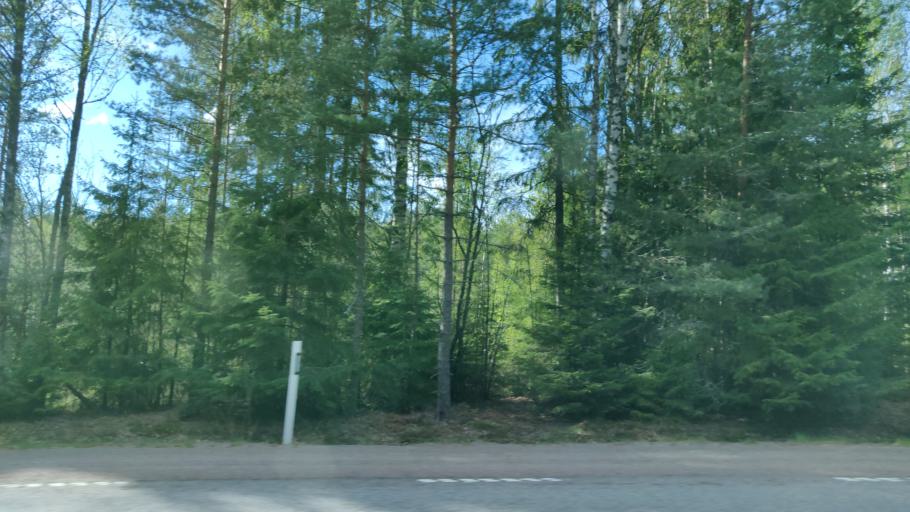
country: SE
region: Vaermland
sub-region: Forshaga Kommun
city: Forshaga
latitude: 59.4850
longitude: 13.4153
